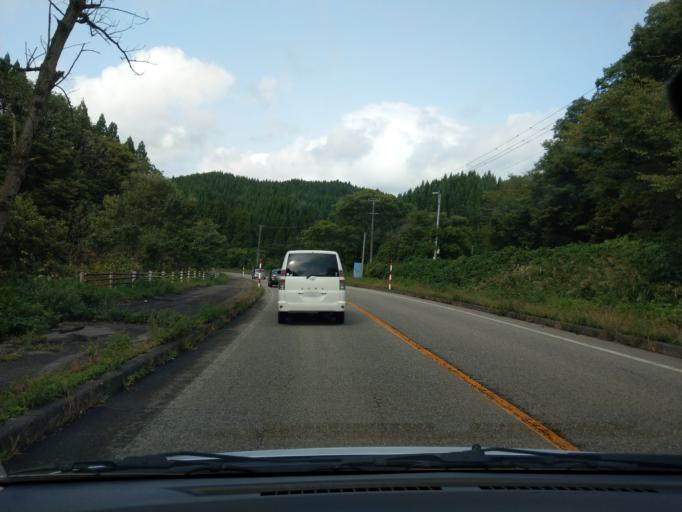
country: JP
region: Akita
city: Omagari
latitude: 39.4340
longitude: 140.3764
